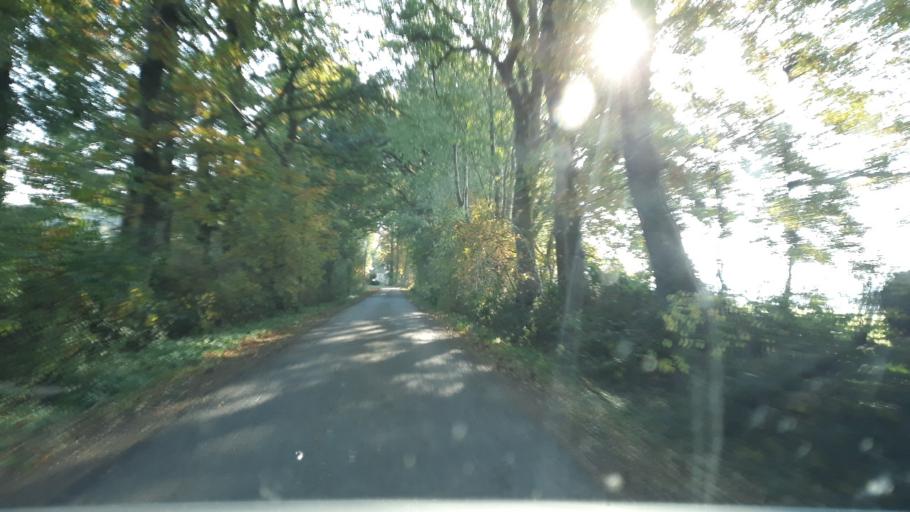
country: DE
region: Schleswig-Holstein
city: Borm
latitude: 54.4037
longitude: 9.3854
